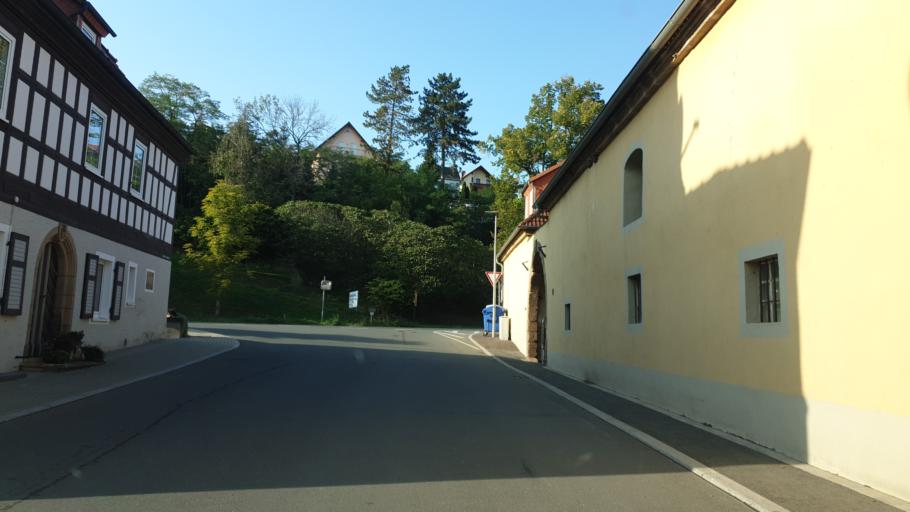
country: DE
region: Thuringia
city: Hartmannsdorf
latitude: 50.9606
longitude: 11.9758
